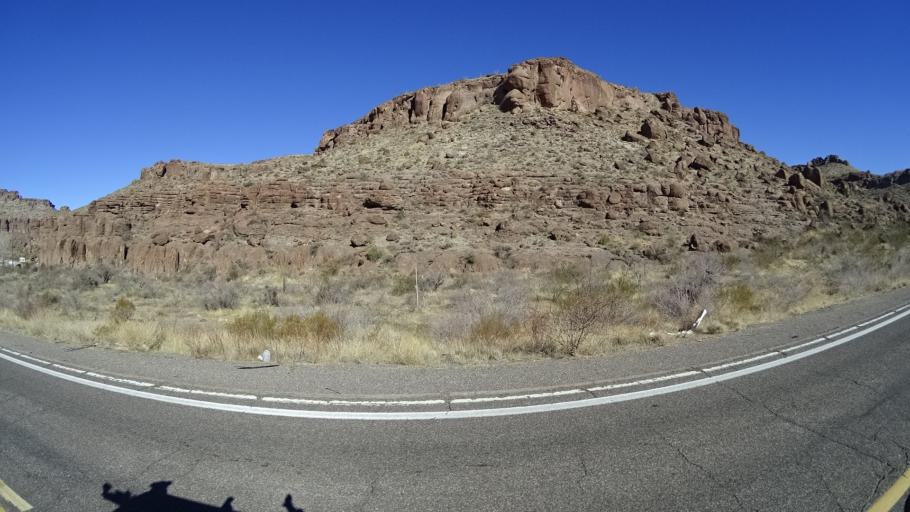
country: US
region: Arizona
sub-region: Mohave County
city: Kingman
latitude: 35.1637
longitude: -114.0665
